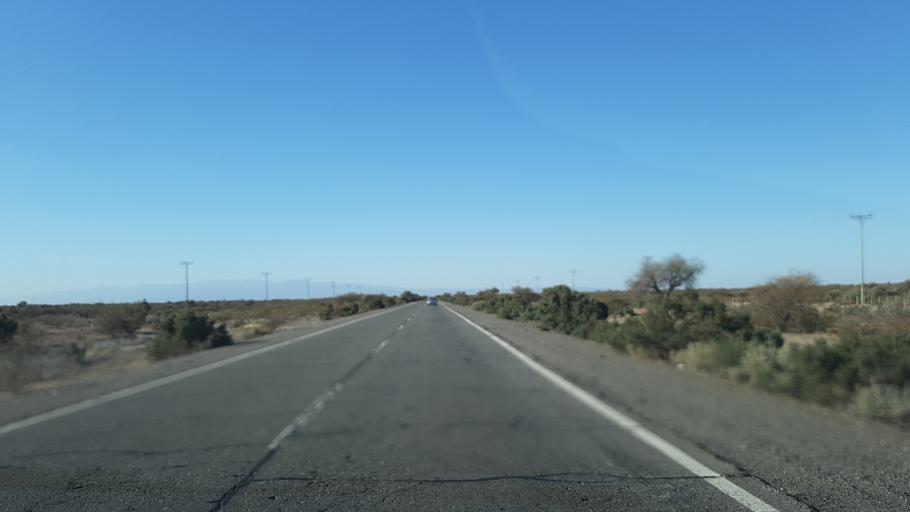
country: AR
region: San Juan
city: Caucete
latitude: -31.6319
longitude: -67.7447
